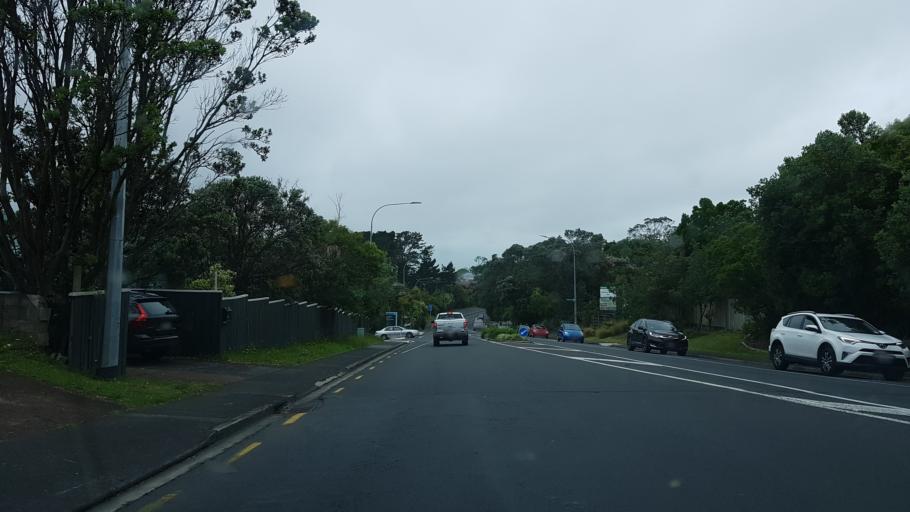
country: NZ
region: Auckland
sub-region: Auckland
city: North Shore
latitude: -36.8111
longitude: 174.7207
